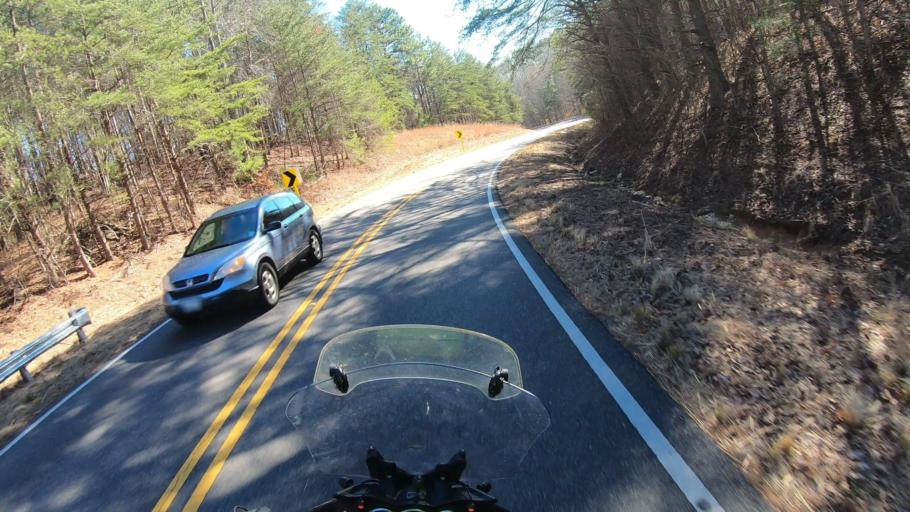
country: US
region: Alabama
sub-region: Calhoun County
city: Oxford
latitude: 33.4818
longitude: -85.7913
